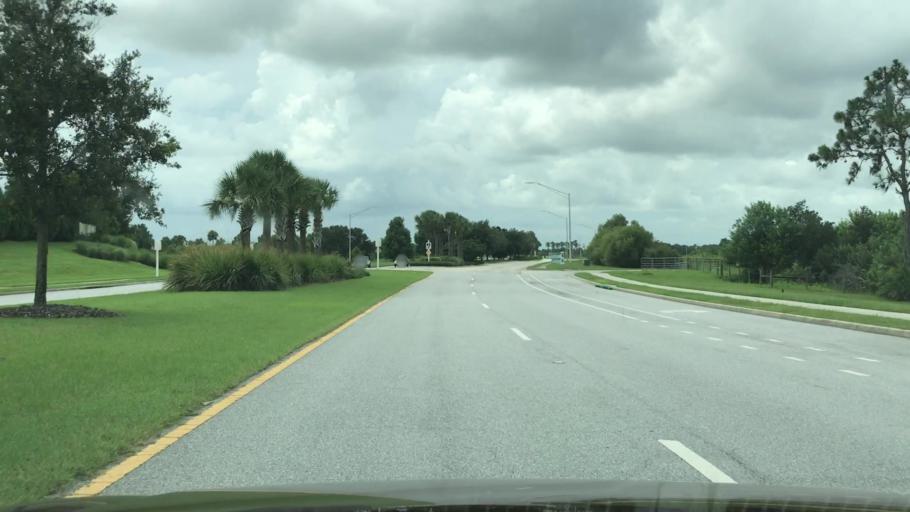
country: US
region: Florida
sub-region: Sarasota County
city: The Meadows
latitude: 27.4473
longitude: -82.4162
